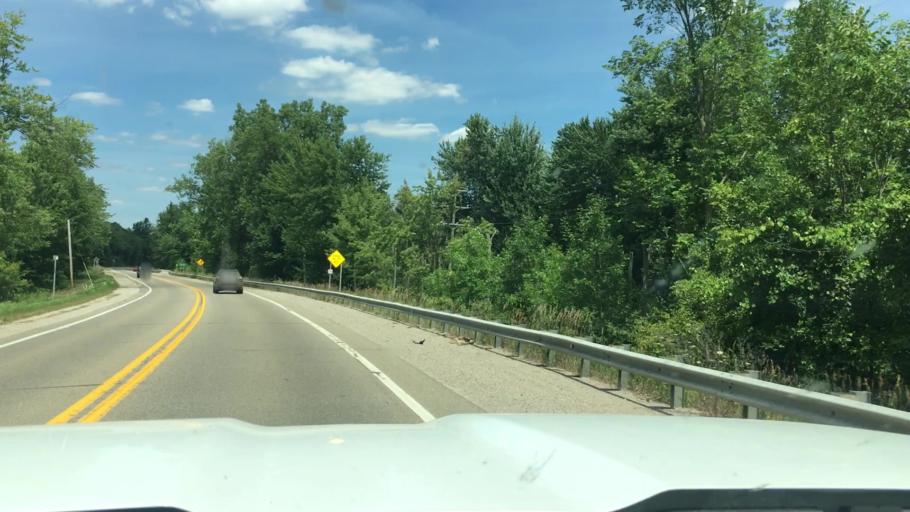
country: US
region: Michigan
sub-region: Lapeer County
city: Barnes Lake-Millers Lake
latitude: 43.2091
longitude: -83.3133
